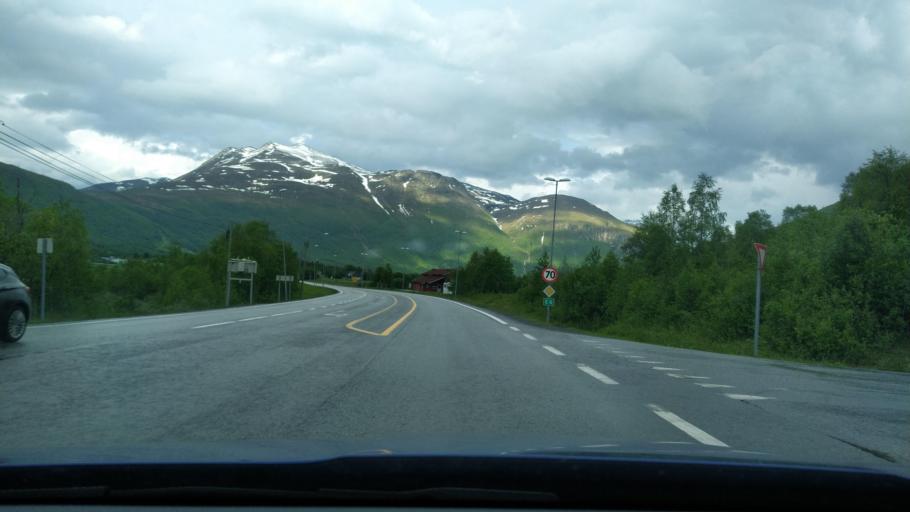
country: NO
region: Troms
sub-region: Balsfjord
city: Storsteinnes
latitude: 69.2130
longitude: 19.5358
